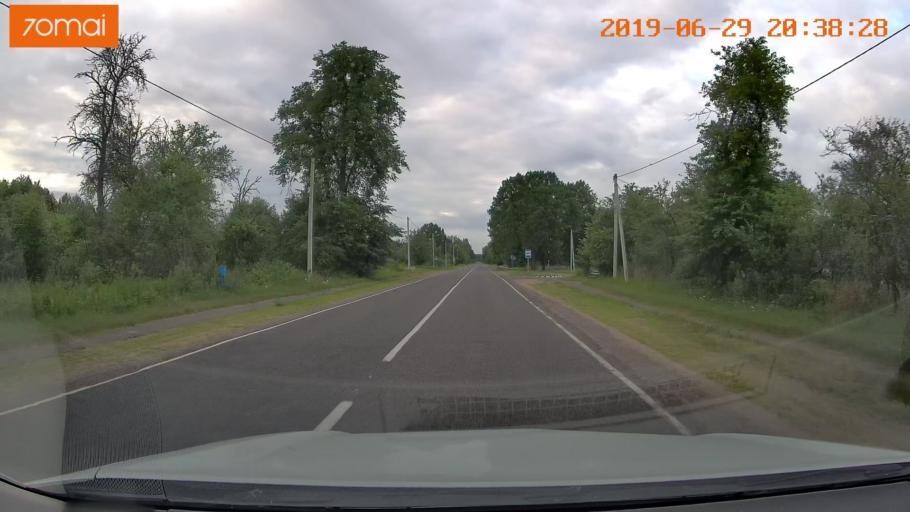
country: BY
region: Brest
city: Hantsavichy
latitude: 52.5503
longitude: 26.3646
